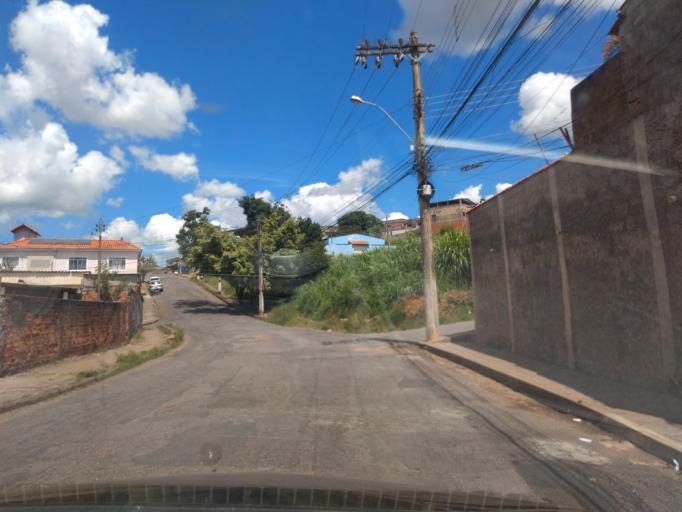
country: BR
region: Minas Gerais
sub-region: Tres Coracoes
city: Tres Coracoes
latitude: -21.6858
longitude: -45.2524
